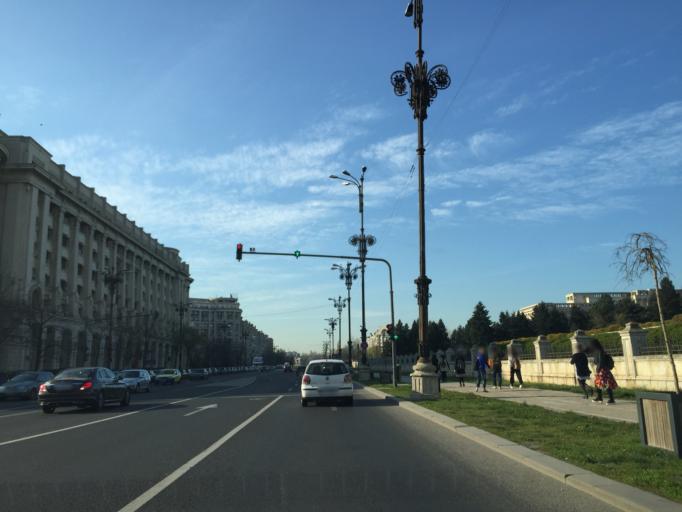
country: RO
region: Bucuresti
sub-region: Municipiul Bucuresti
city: Bucuresti
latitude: 44.4267
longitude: 26.0907
